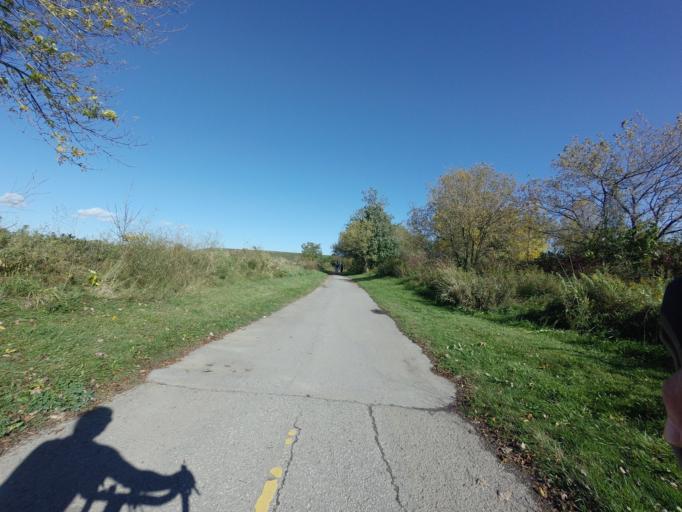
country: CA
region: Ontario
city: Oshawa
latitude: 43.8498
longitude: -78.9179
